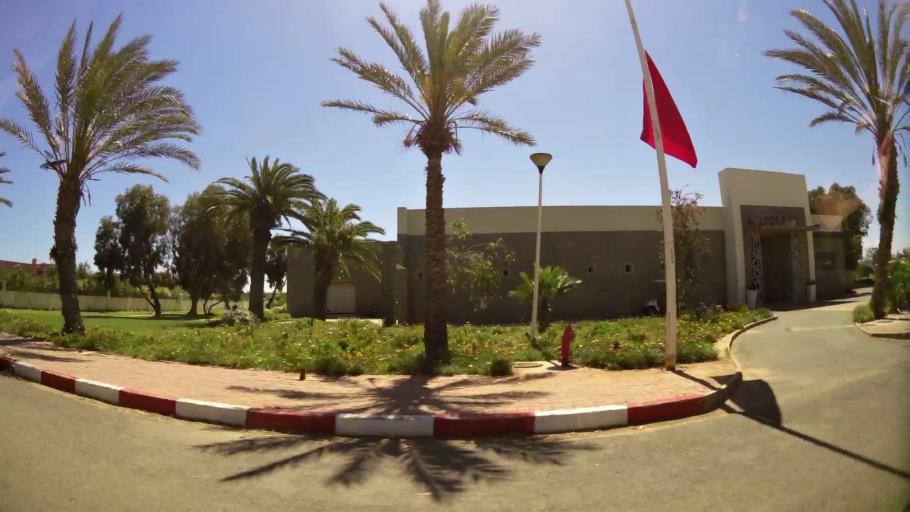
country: MA
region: Oriental
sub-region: Berkane-Taourirt
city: Madagh
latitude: 35.1108
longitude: -2.3101
